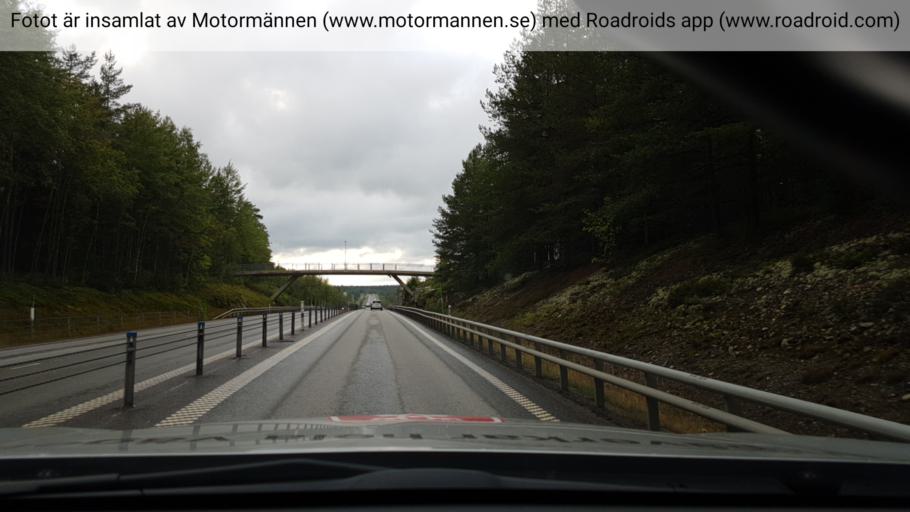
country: SE
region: Vaesterbotten
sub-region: Umea Kommun
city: Ersmark
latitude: 63.8478
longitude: 20.3306
